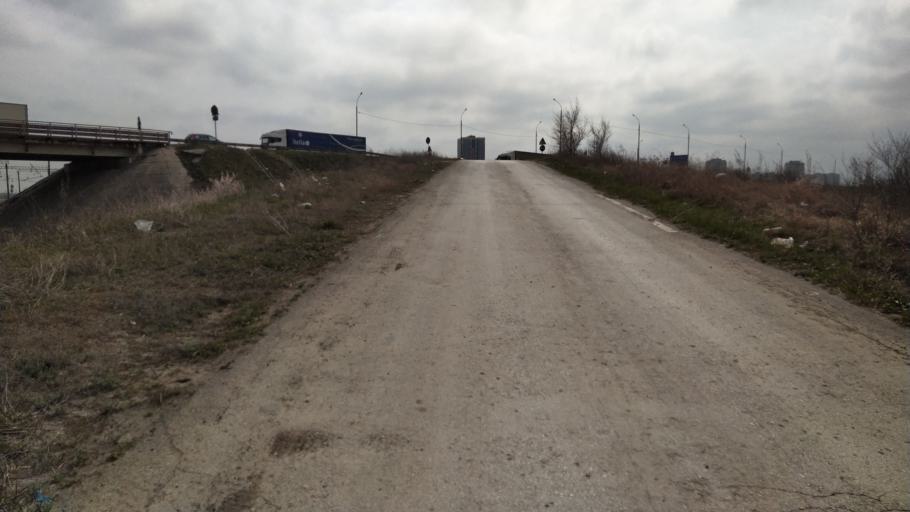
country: RU
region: Rostov
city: Bataysk
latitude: 47.1662
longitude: 39.7425
